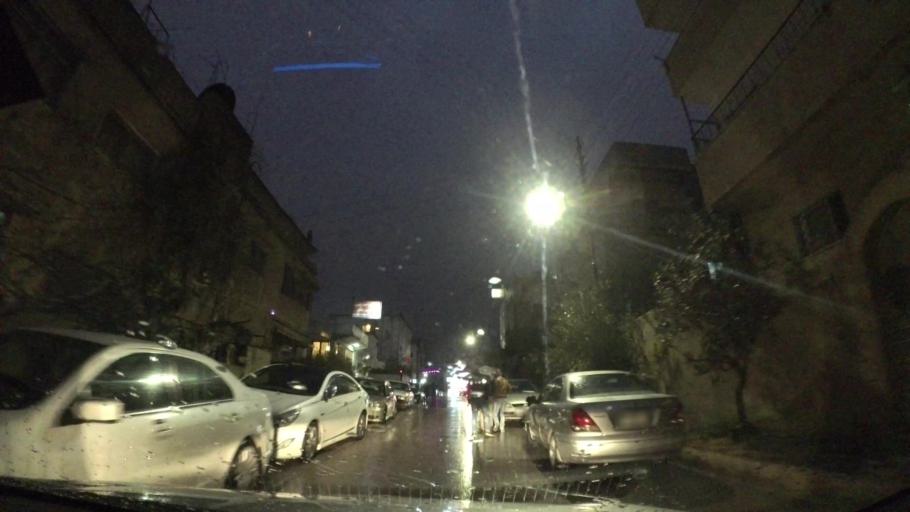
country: JO
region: Amman
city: Al Jubayhah
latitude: 32.0244
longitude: 35.8469
